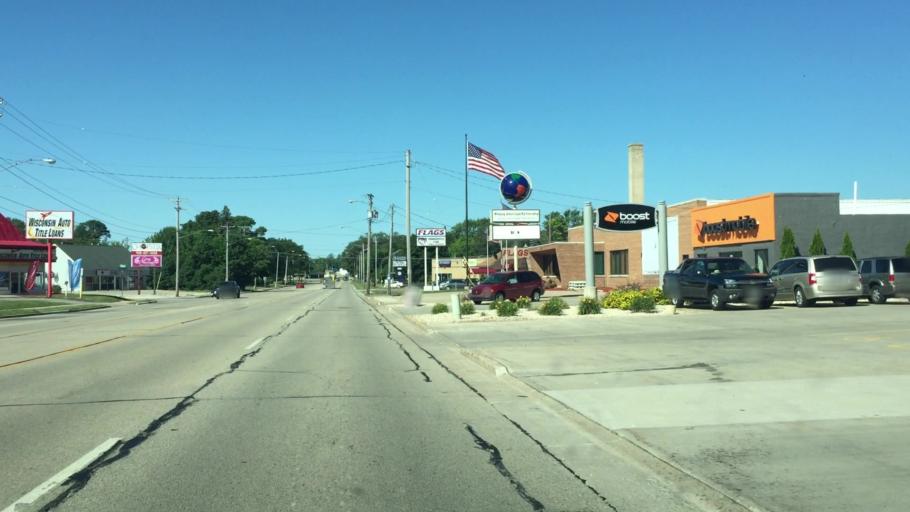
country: US
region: Wisconsin
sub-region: Outagamie County
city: Appleton
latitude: 44.2415
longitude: -88.4180
